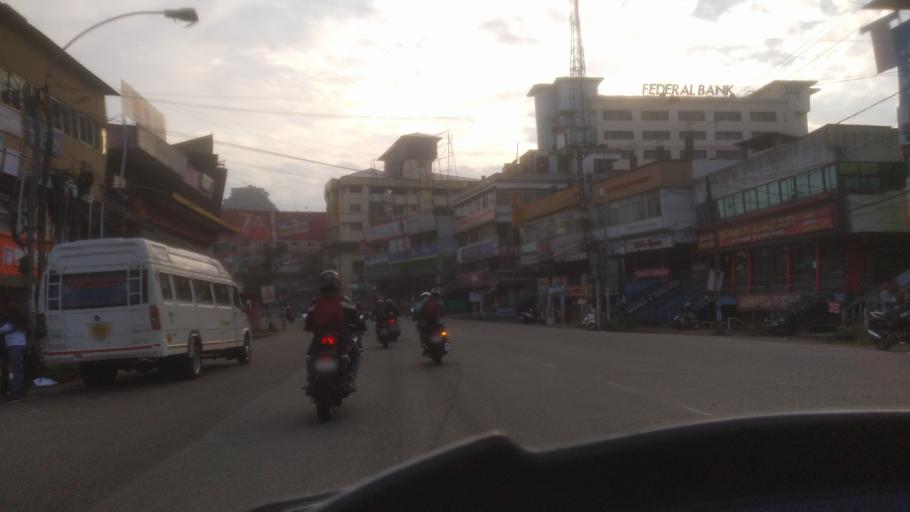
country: IN
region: Kerala
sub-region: Ernakulam
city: Aluva
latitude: 10.1107
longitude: 76.3495
